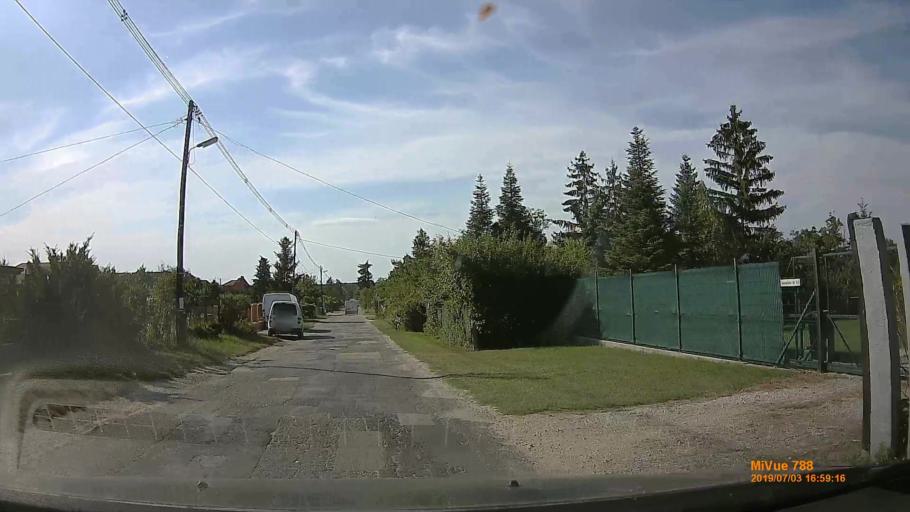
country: HU
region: Gyor-Moson-Sopron
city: Gyor
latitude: 47.7196
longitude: 17.7136
